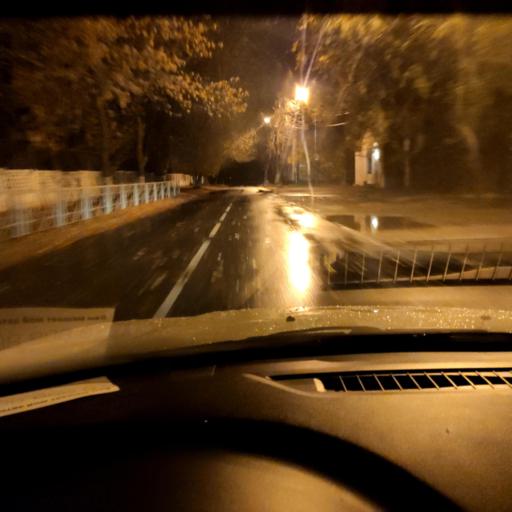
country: RU
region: Samara
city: Tol'yatti
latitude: 53.5112
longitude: 49.4046
